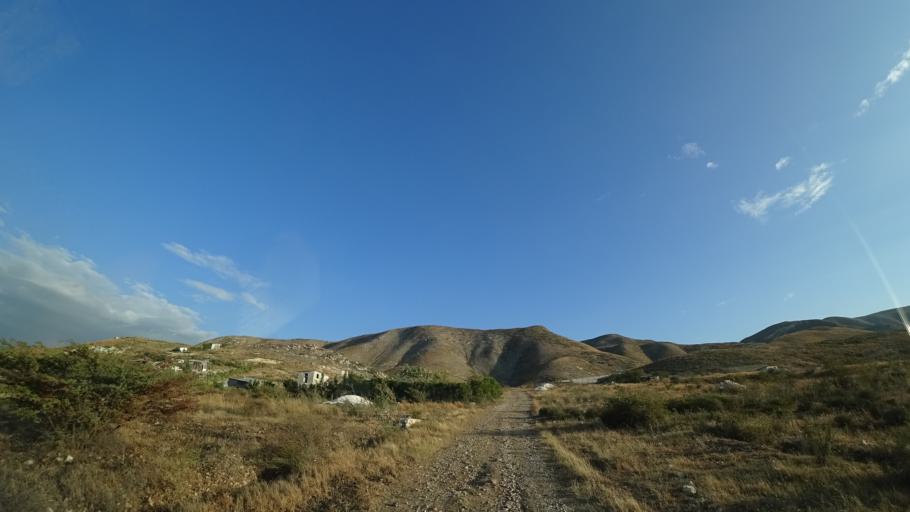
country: HT
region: Ouest
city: Croix des Bouquets
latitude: 18.6788
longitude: -72.2933
